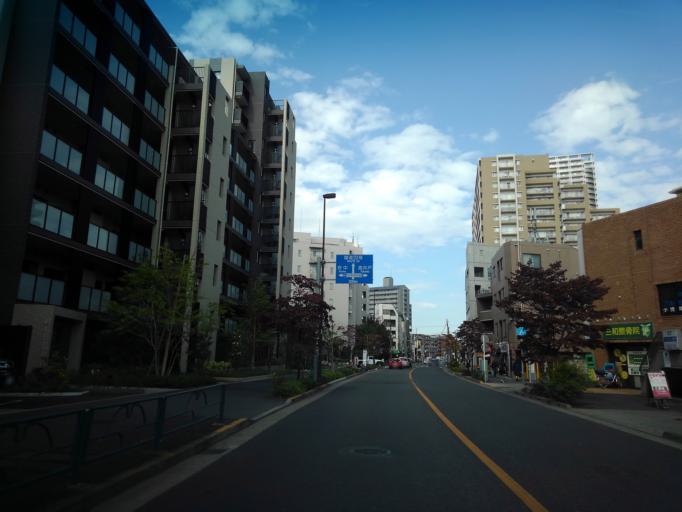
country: JP
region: Tokyo
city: Chofugaoka
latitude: 35.6480
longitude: 139.5595
